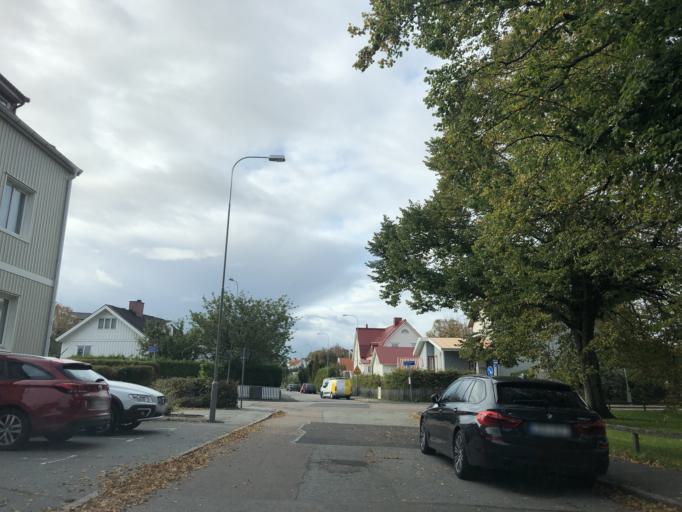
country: SE
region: Vaestra Goetaland
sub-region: Goteborg
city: Majorna
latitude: 57.6765
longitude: 11.8780
